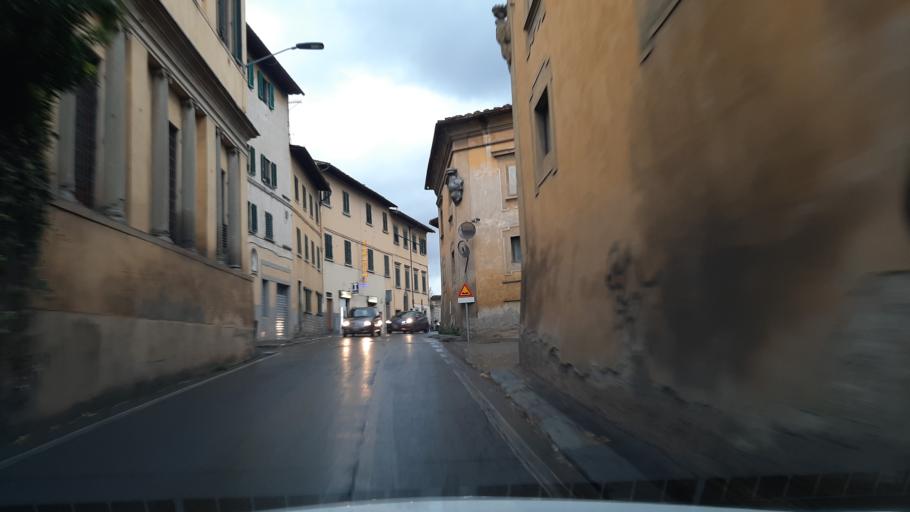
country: IT
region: Tuscany
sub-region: Province of Florence
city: Florence
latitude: 43.7977
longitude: 11.2622
